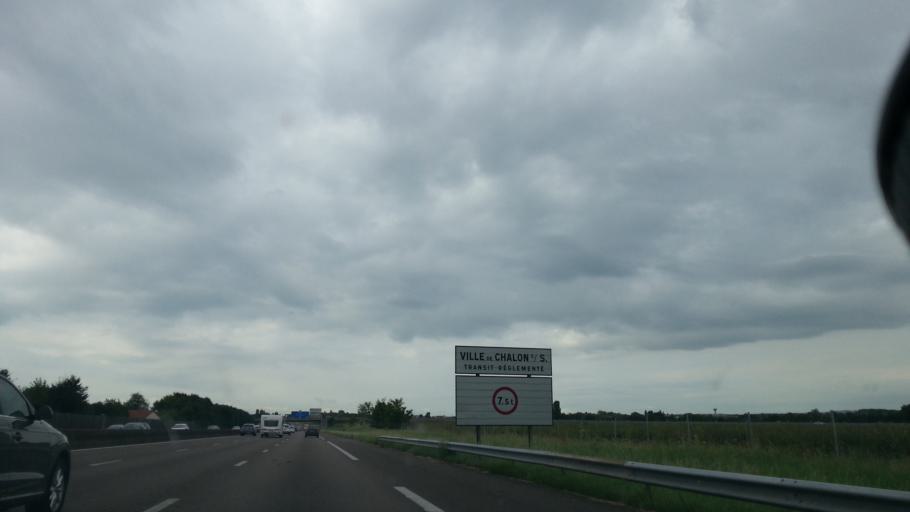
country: FR
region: Bourgogne
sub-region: Departement de Saone-et-Loire
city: Champforgeuil
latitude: 46.8137
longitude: 4.8277
